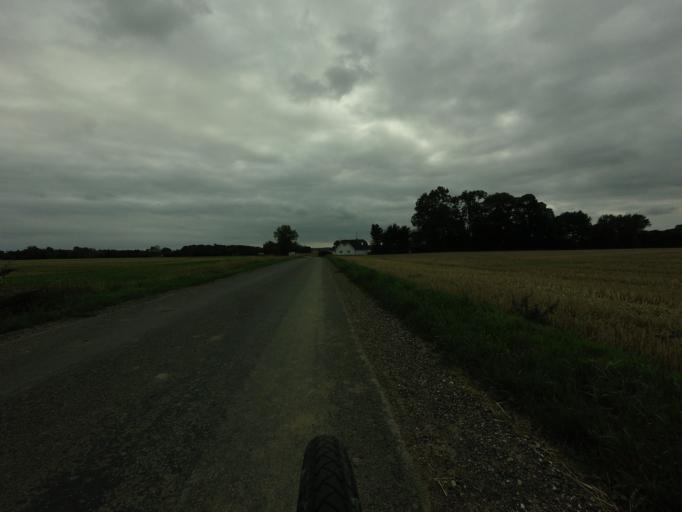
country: DK
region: Zealand
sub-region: Stevns Kommune
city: Store Heddinge
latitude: 55.3383
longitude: 12.3332
